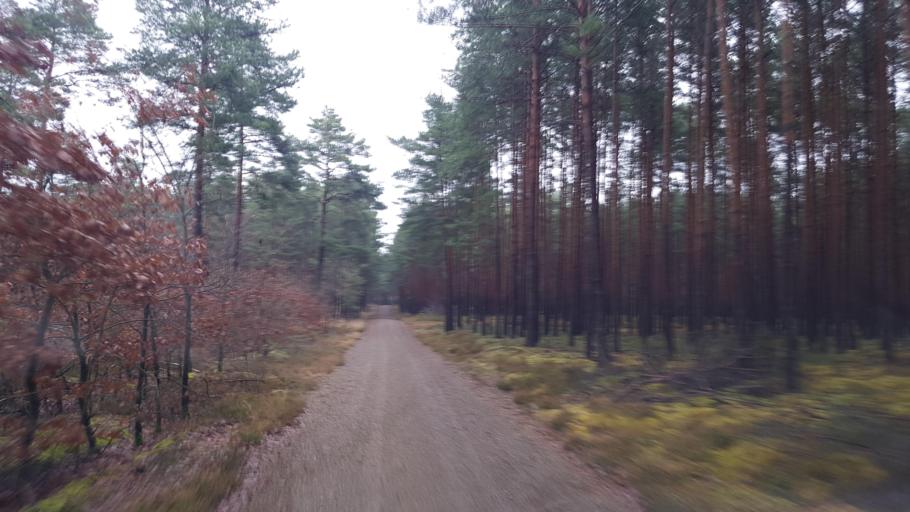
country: DE
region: Brandenburg
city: Grossraschen
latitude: 51.6354
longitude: 13.9718
